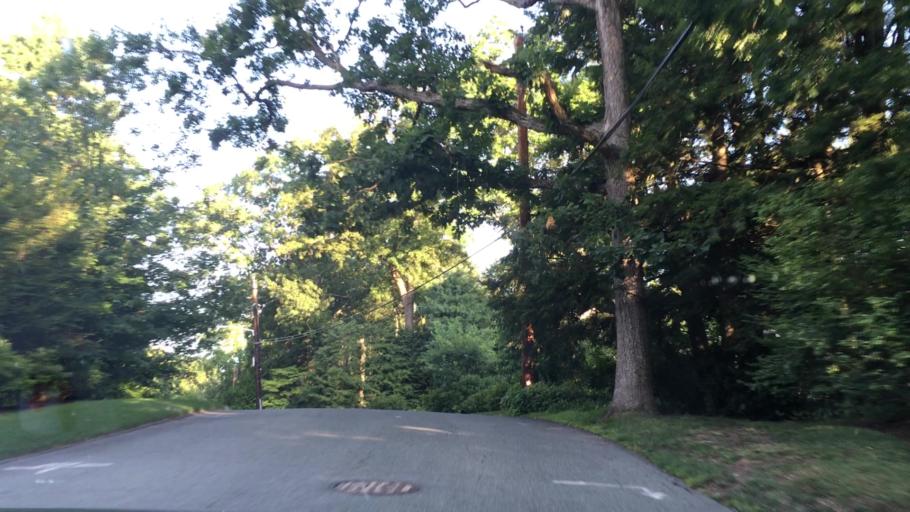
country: US
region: Massachusetts
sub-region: Norfolk County
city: Wellesley
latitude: 42.3116
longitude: -71.2856
